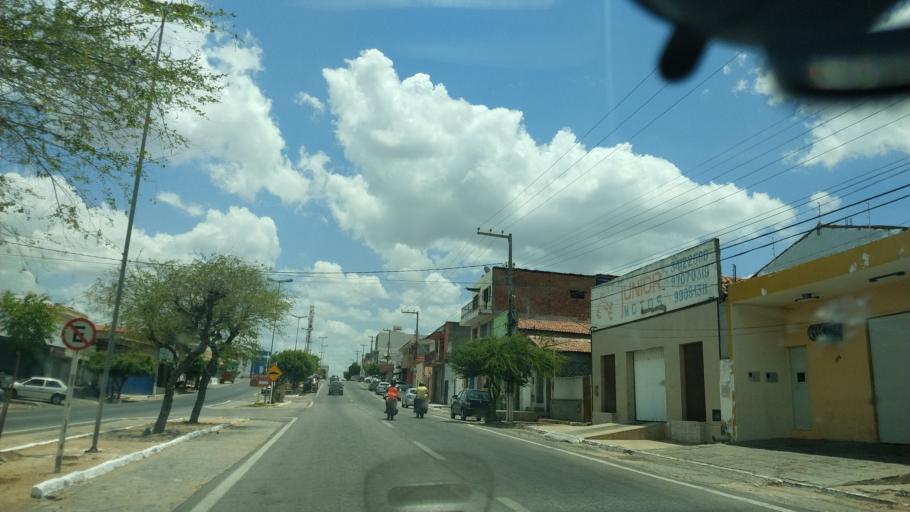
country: BR
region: Rio Grande do Norte
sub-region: Currais Novos
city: Currais Novos
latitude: -6.2587
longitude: -36.5136
